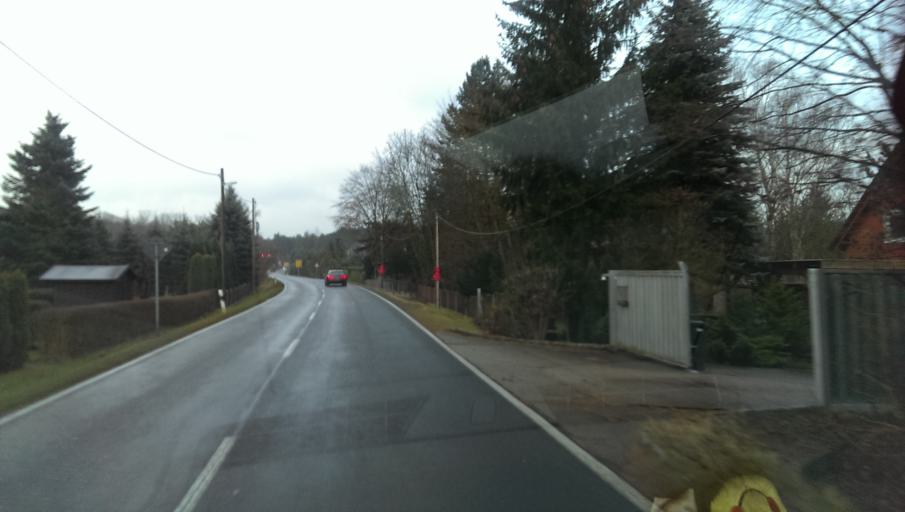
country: DE
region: Saxony
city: Moritzburg
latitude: 51.1620
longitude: 13.6295
